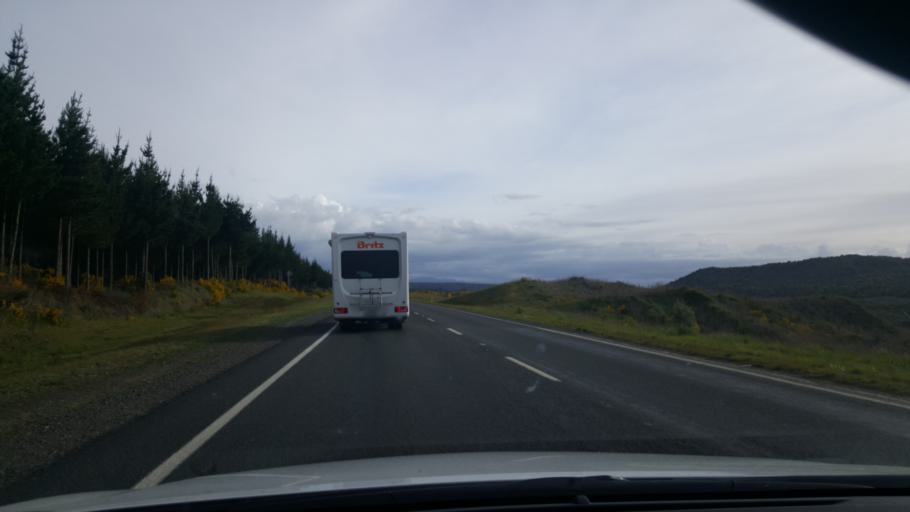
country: NZ
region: Waikato
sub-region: Taupo District
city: Taupo
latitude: -38.8318
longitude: 176.0658
